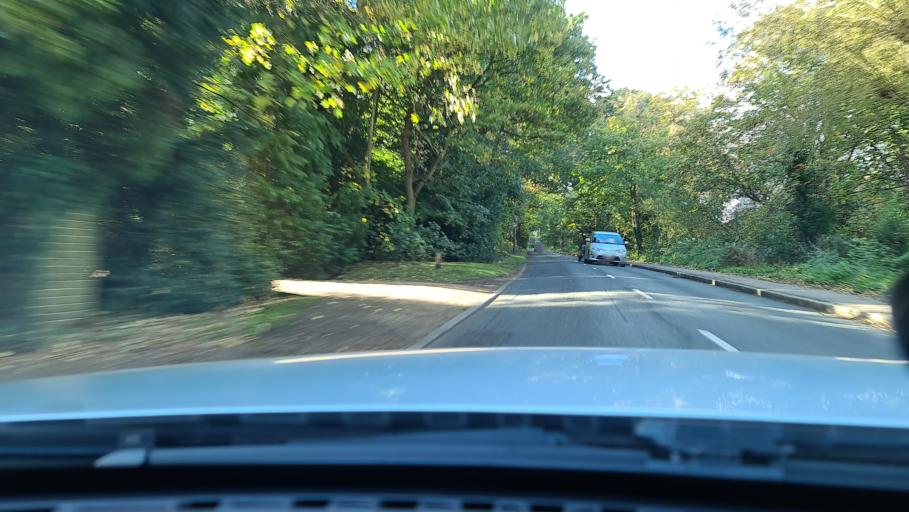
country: GB
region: England
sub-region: Surrey
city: Walton-on-Thames
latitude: 51.3696
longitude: -0.4146
